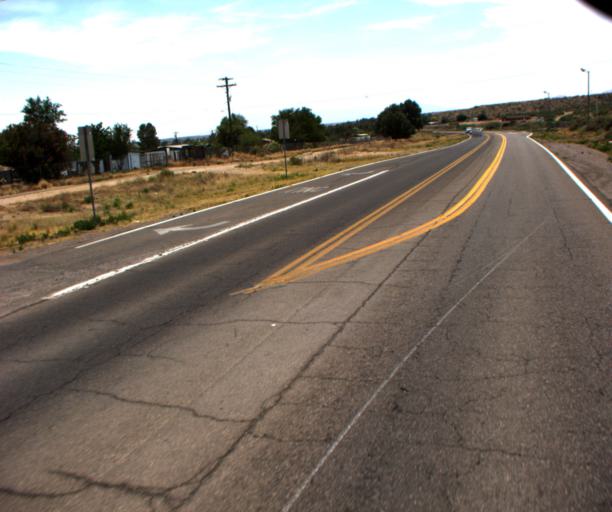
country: US
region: Arizona
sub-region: Graham County
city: Bylas
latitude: 33.1432
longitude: -110.1257
